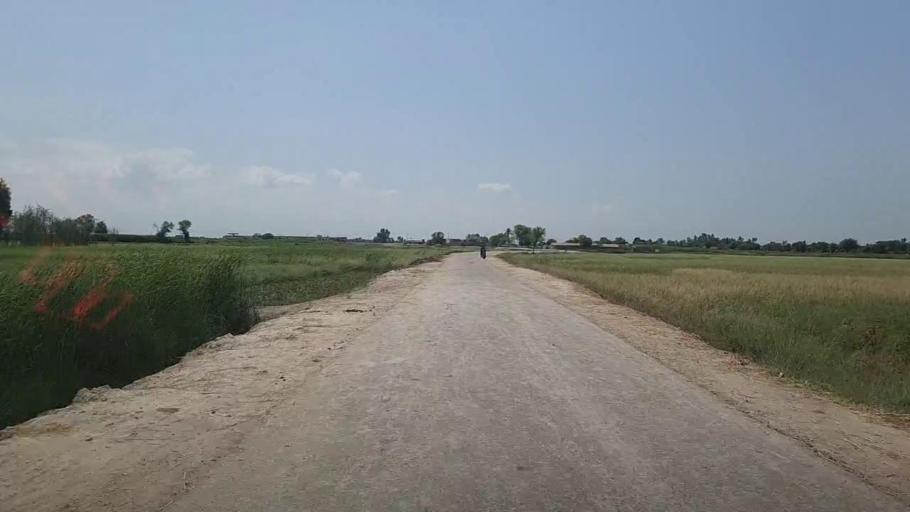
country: PK
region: Sindh
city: Ubauro
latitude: 28.1888
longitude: 69.7999
